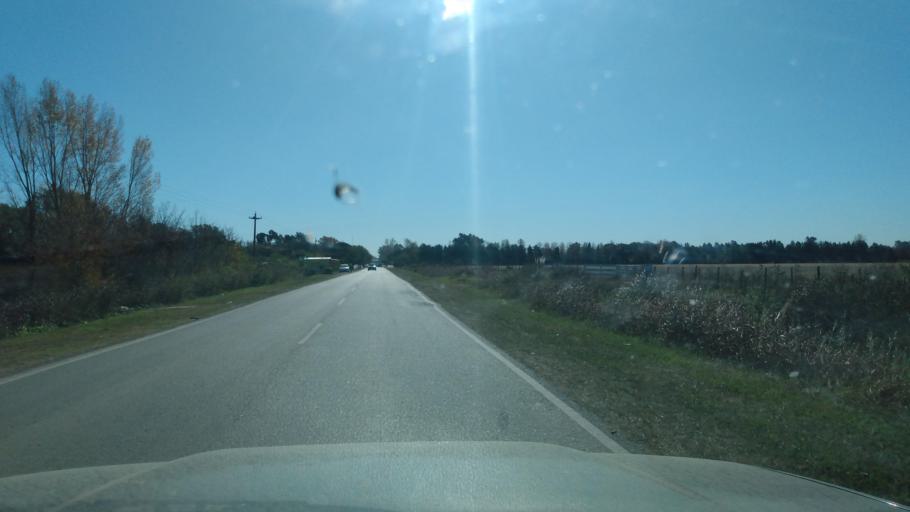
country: AR
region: Buenos Aires
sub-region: Partido de Lujan
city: Lujan
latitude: -34.4922
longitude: -59.2101
